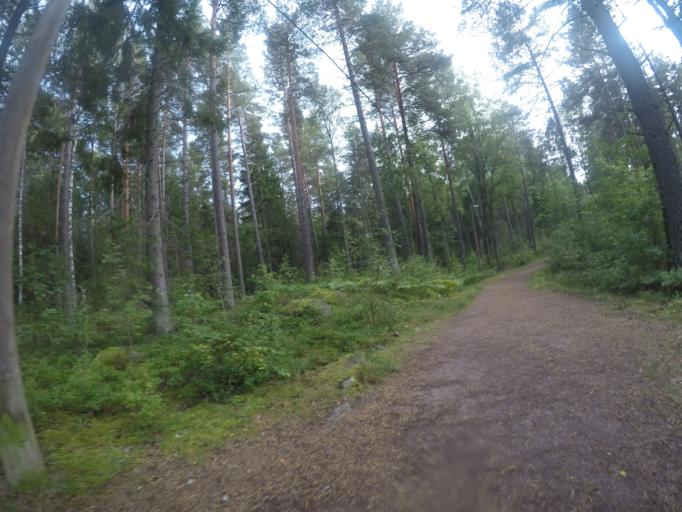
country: SE
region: Vaestmanland
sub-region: Vasteras
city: Vasteras
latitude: 59.6501
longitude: 16.5192
